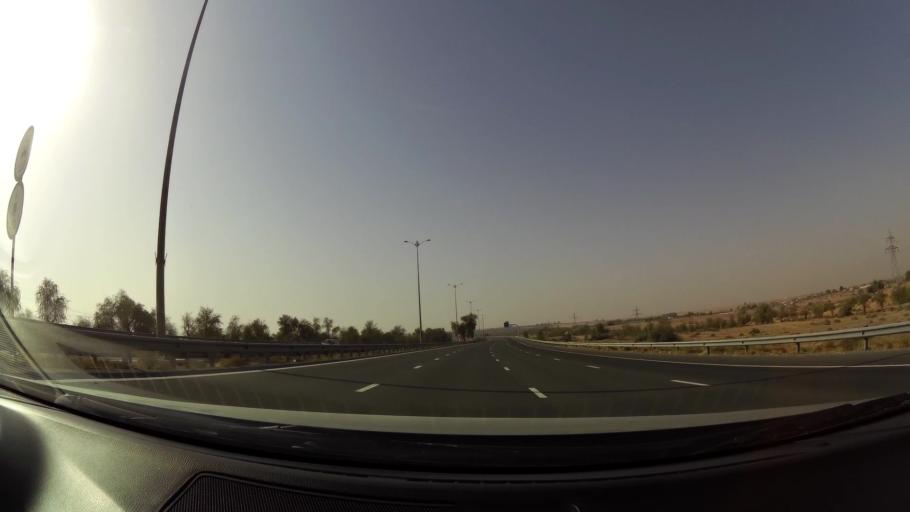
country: OM
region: Al Buraimi
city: Al Buraymi
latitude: 24.6496
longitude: 55.7035
